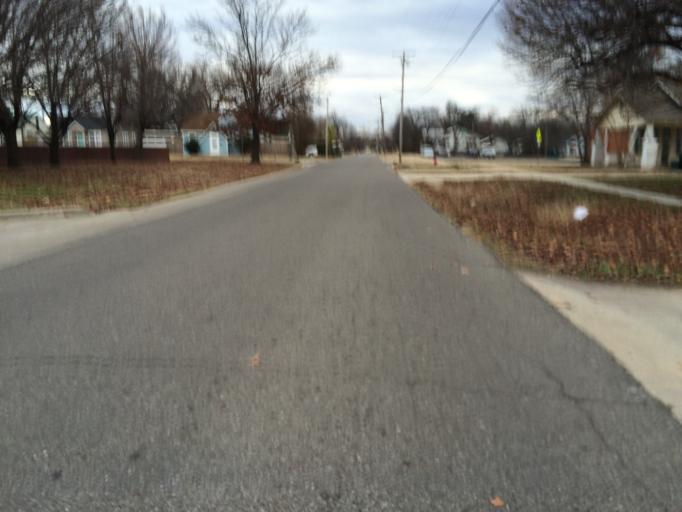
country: US
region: Oklahoma
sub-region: Cleveland County
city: Norman
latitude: 35.2292
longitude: -97.4427
